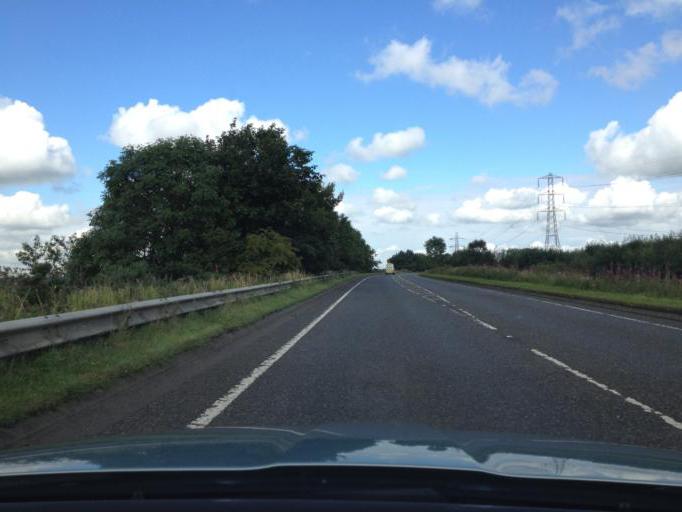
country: GB
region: Scotland
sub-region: West Lothian
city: Whitburn
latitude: 55.8864
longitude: -3.6715
